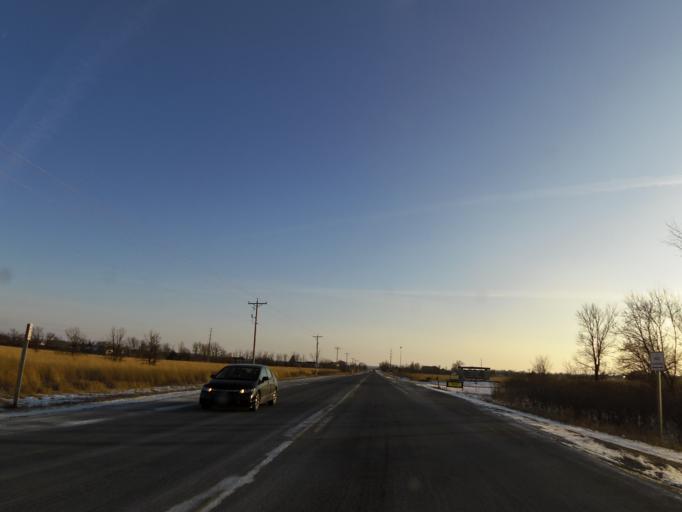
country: US
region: Wisconsin
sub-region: Saint Croix County
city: North Hudson
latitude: 45.0136
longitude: -92.6756
